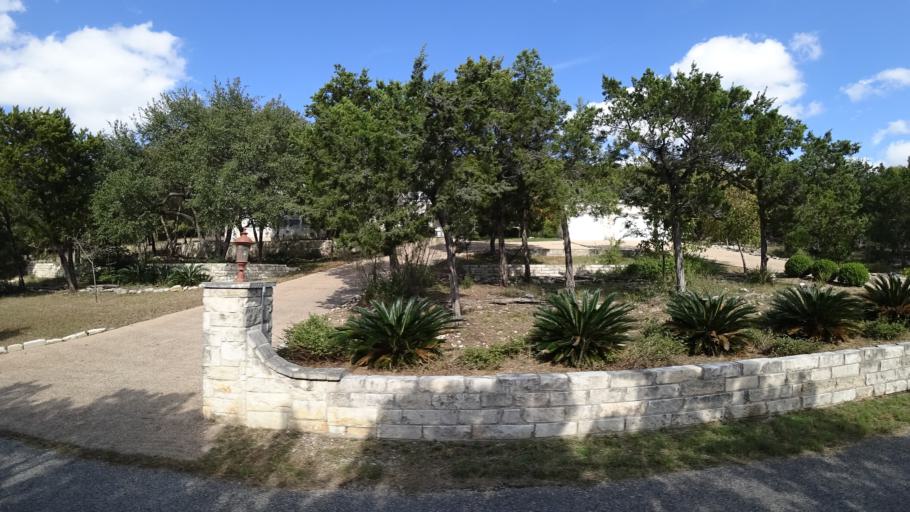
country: US
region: Texas
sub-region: Williamson County
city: Anderson Mill
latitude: 30.4197
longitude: -97.8037
